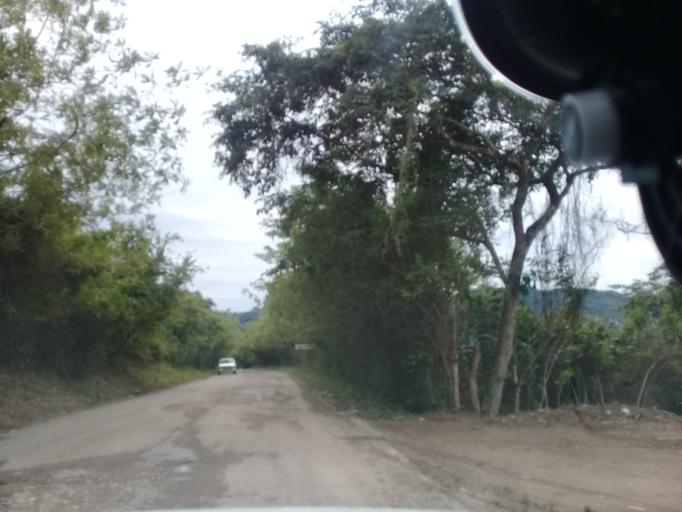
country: MX
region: Veracruz
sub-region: Chalma
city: San Pedro Coyutla
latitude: 21.2118
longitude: -98.3849
